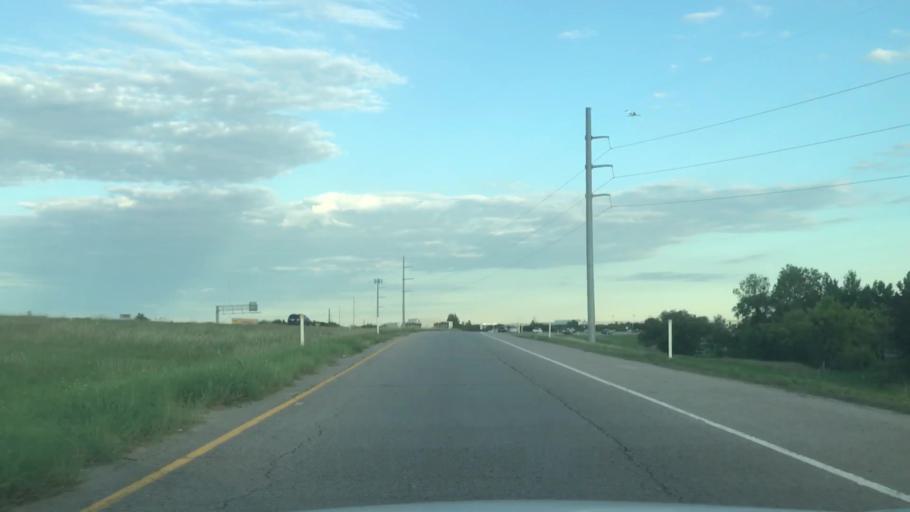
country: US
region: Texas
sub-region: Dallas County
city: Coppell
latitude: 32.9441
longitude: -97.0201
